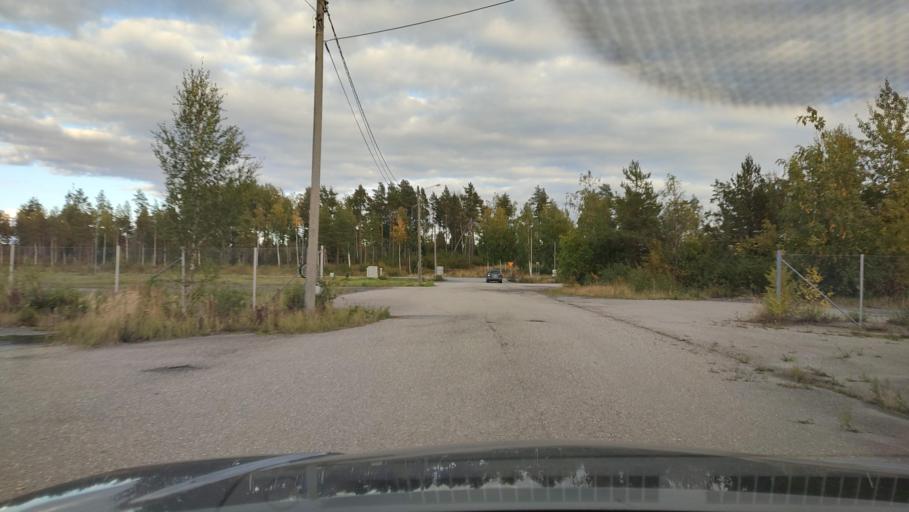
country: FI
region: Ostrobothnia
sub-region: Sydosterbotten
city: Kristinestad
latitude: 62.2647
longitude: 21.3819
